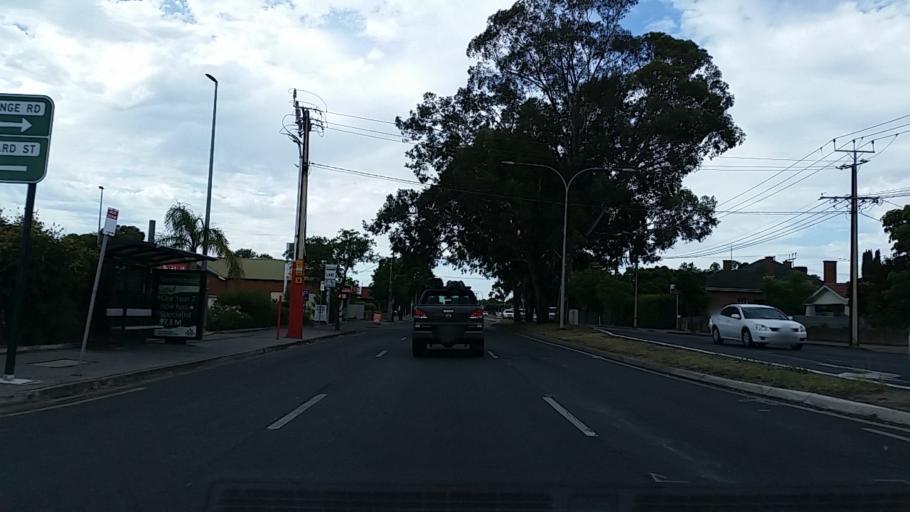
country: AU
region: South Australia
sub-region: Mitcham
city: Clarence Gardens
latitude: -34.9795
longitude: 138.5917
